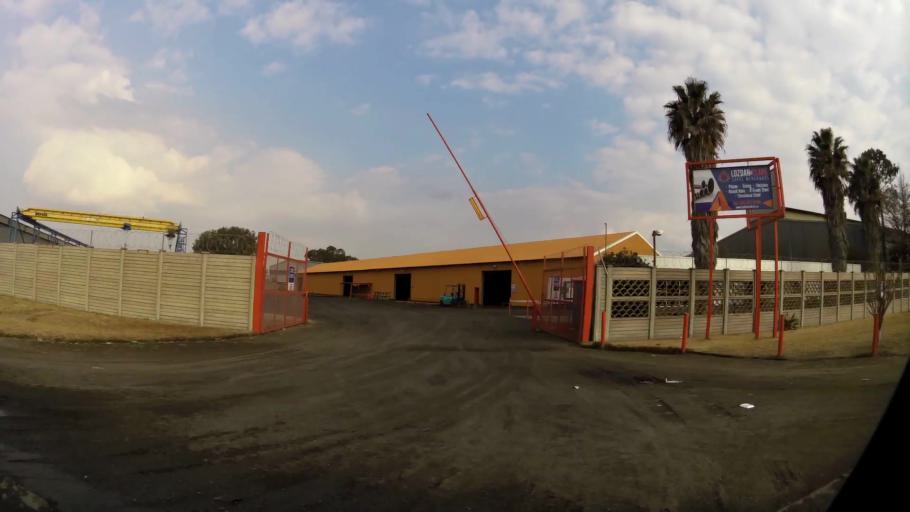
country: ZA
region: Gauteng
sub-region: Sedibeng District Municipality
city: Vereeniging
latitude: -26.6844
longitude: 27.9098
